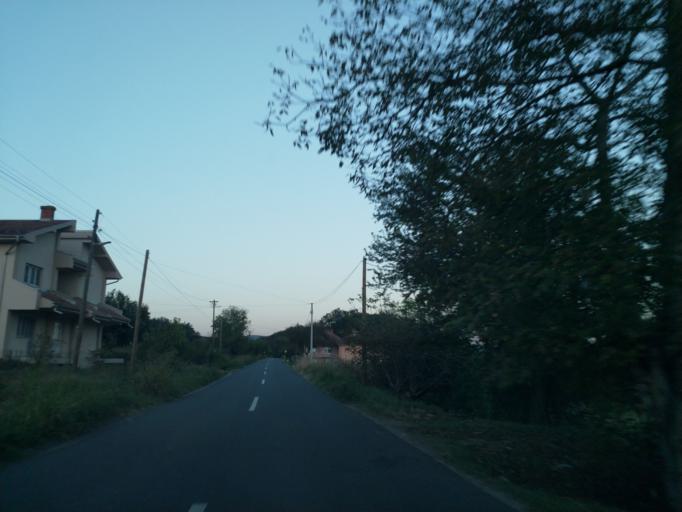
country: RS
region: Central Serbia
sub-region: Rasinski Okrug
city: Krusevac
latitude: 43.6211
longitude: 21.3135
